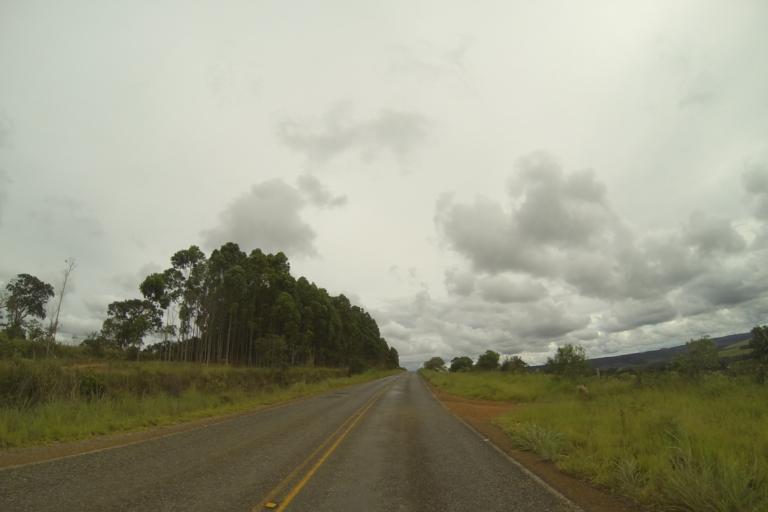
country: BR
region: Minas Gerais
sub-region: Ibia
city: Ibia
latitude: -19.6904
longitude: -46.4431
